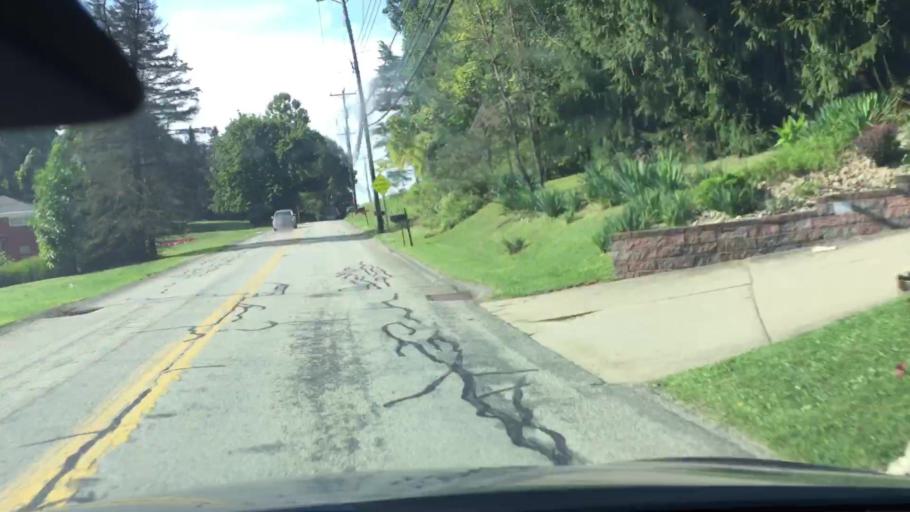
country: US
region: Pennsylvania
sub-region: Allegheny County
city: Pitcairn
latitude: 40.4198
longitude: -79.7631
